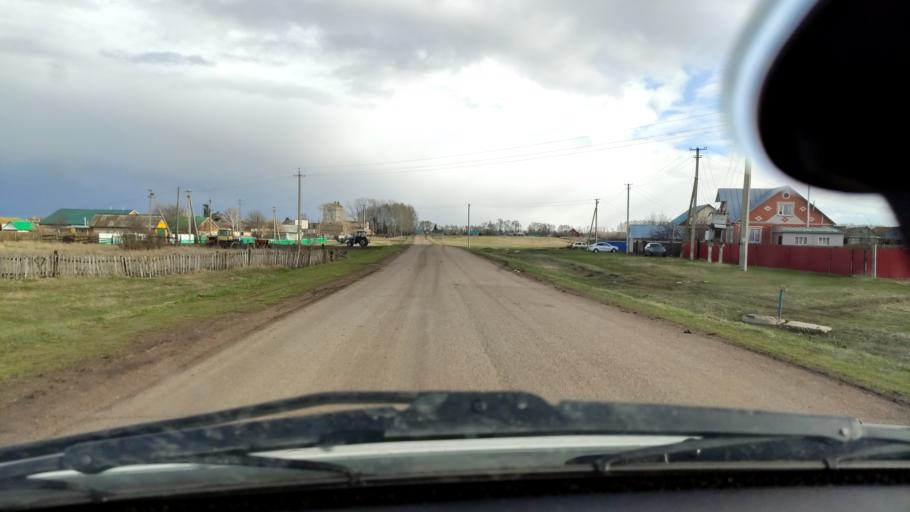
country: RU
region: Bashkortostan
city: Buzdyak
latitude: 54.7673
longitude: 54.6009
